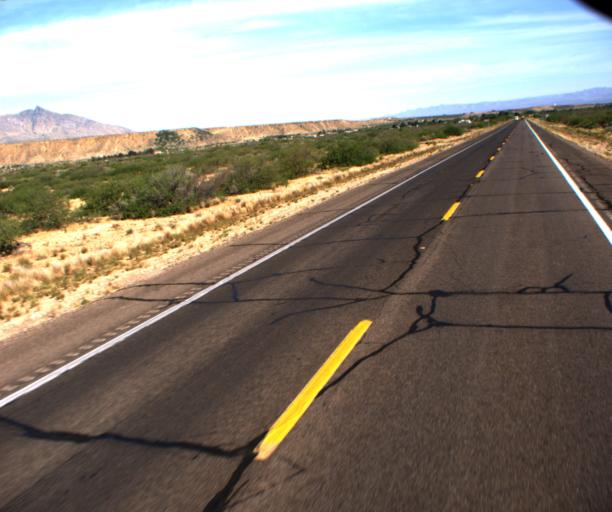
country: US
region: Arizona
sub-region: Graham County
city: Swift Trail Junction
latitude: 32.6755
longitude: -109.7048
